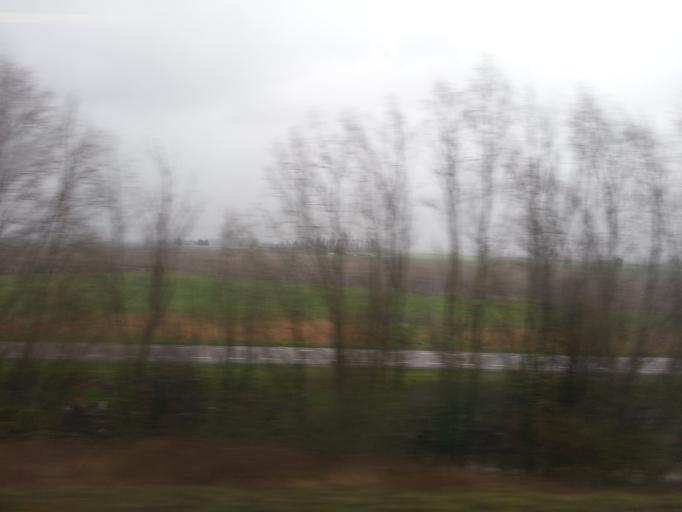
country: NL
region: North Brabant
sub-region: Gemeente Breda
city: Breda
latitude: 51.6409
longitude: 4.6972
